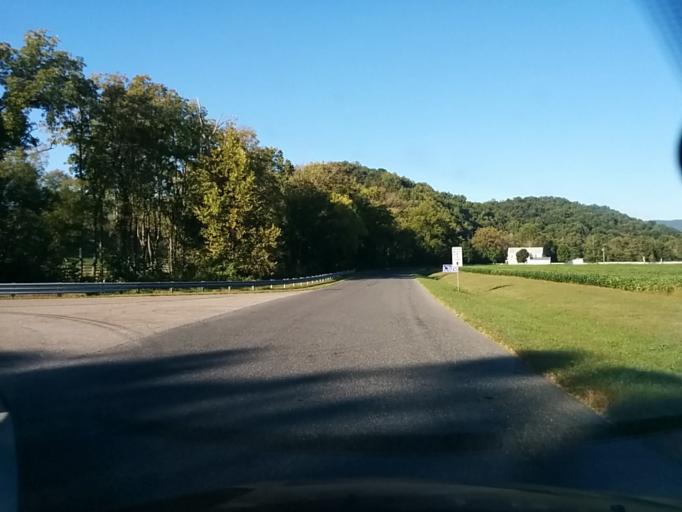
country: US
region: Virginia
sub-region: City of Lexington
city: Lexington
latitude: 37.7403
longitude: -79.5733
